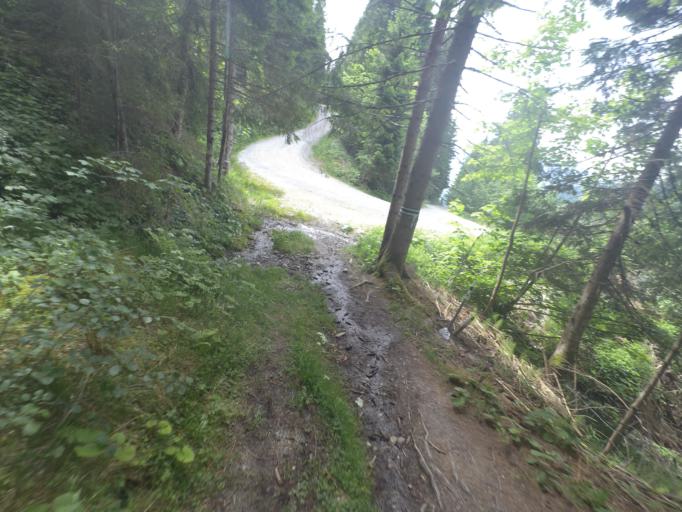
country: AT
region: Salzburg
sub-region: Politischer Bezirk Sankt Johann im Pongau
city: Muhlbach am Hochkonig
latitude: 47.3610
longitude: 13.1111
